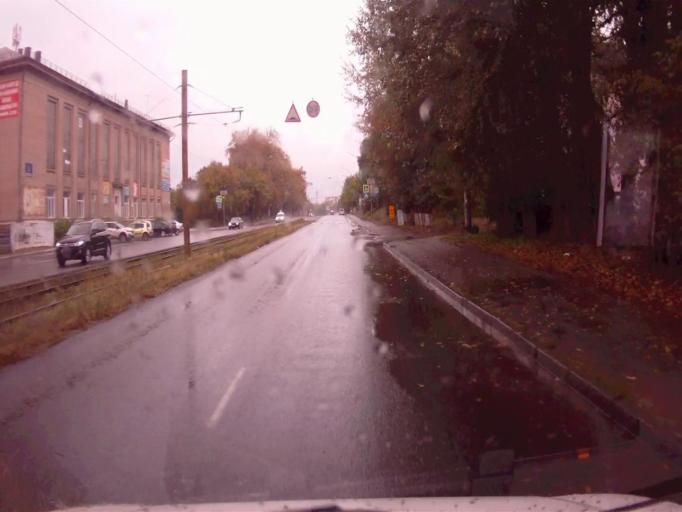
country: RU
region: Chelyabinsk
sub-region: Gorod Chelyabinsk
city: Chelyabinsk
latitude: 55.1800
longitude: 61.4147
